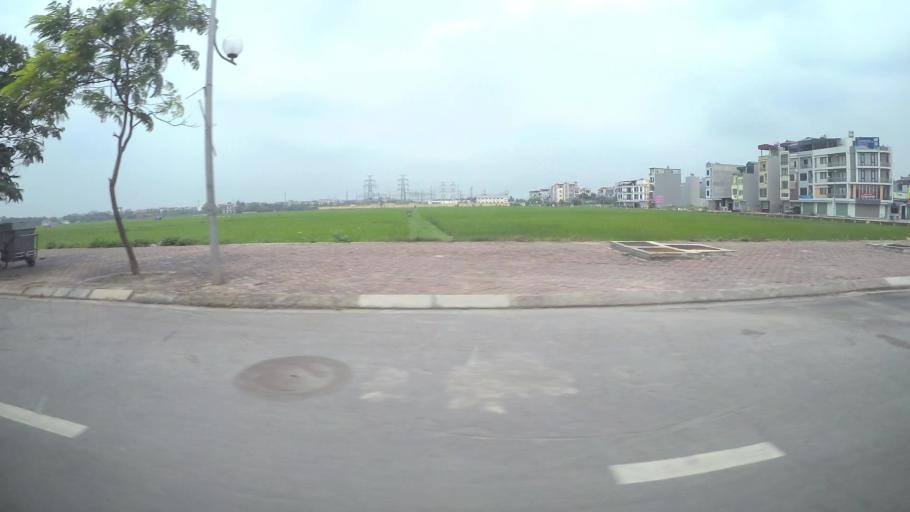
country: VN
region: Ha Noi
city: Trau Quy
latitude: 21.0656
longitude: 105.9119
